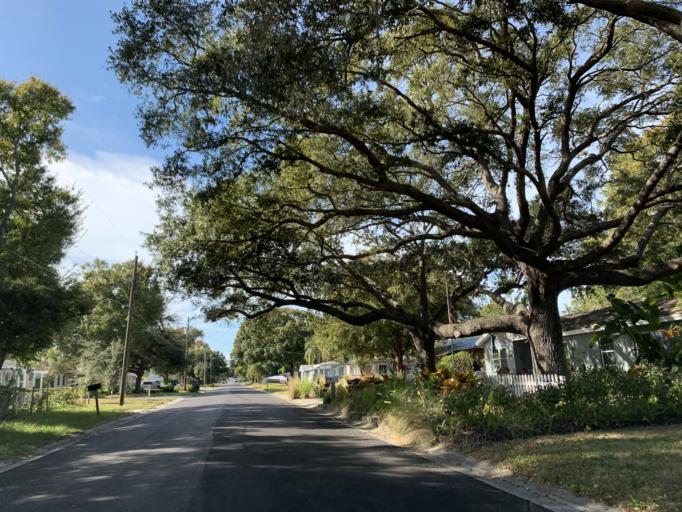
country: US
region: Florida
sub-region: Hillsborough County
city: Tampa
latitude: 27.8861
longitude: -82.5087
